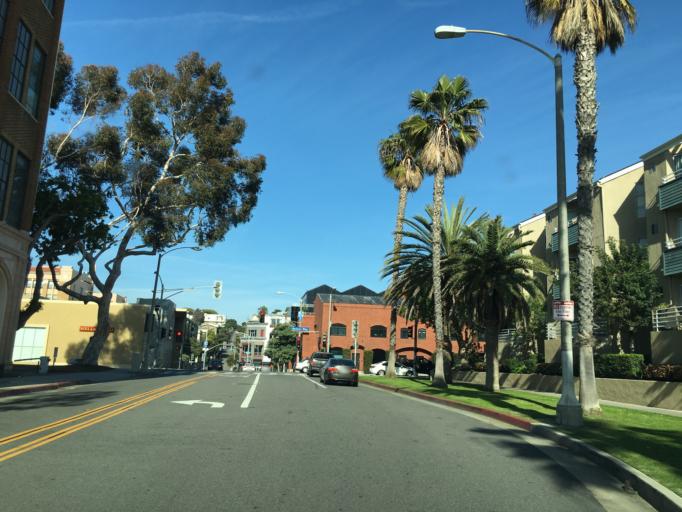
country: US
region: California
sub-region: Los Angeles County
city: Santa Monica
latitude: 33.9972
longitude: -118.4808
